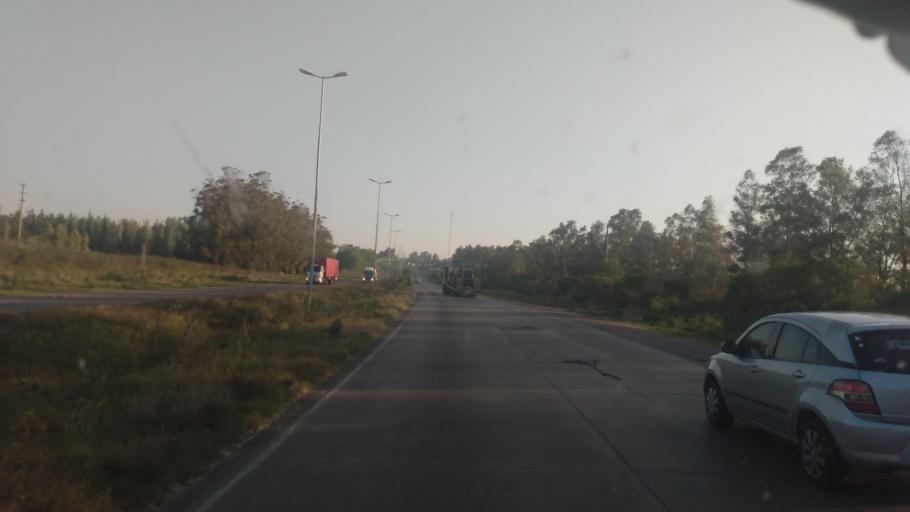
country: AR
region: Buenos Aires
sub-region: Partido de Campana
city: Campana
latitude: -34.2203
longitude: -58.9589
